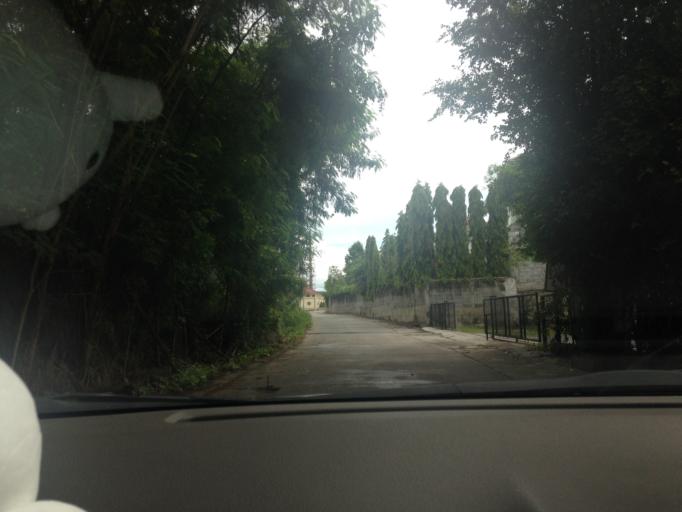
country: TH
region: Chon Buri
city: Chon Buri
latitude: 13.3308
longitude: 100.9246
